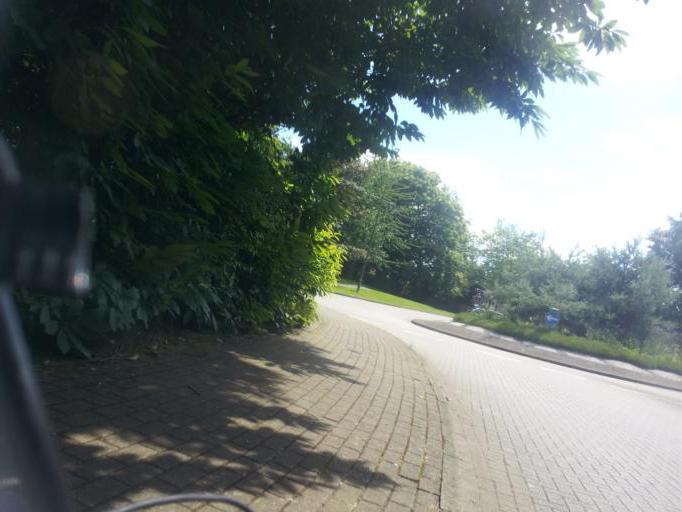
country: GB
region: England
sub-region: Kent
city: Kings Hill
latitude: 51.2708
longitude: 0.3948
